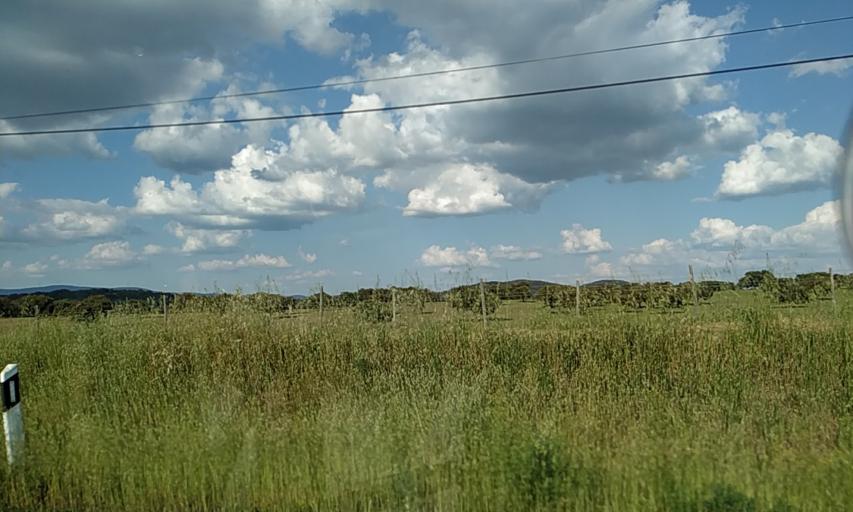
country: PT
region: Portalegre
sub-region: Portalegre
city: Urra
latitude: 39.1940
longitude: -7.4571
